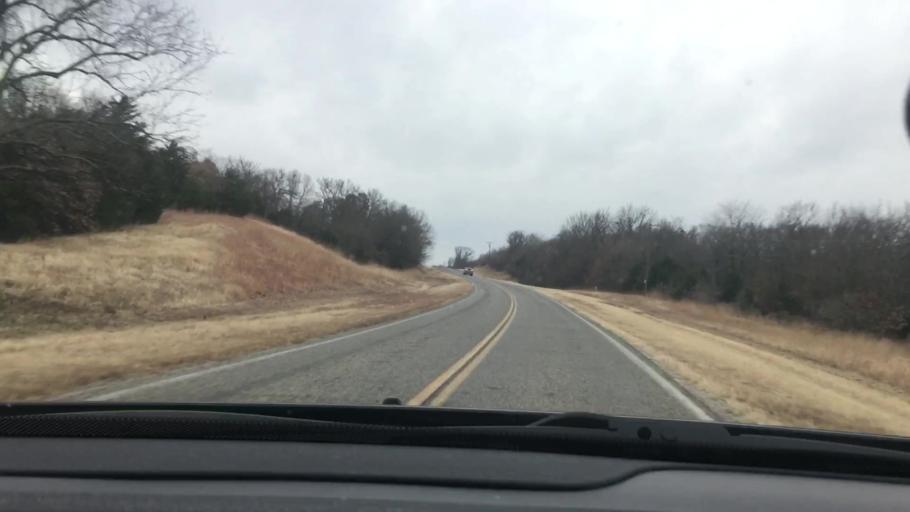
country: US
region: Oklahoma
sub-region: Johnston County
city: Tishomingo
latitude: 34.2252
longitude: -96.6360
